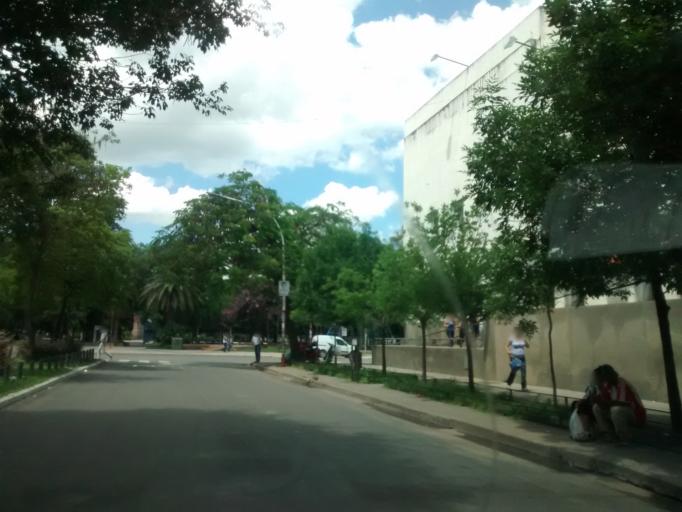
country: AR
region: Chaco
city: Resistencia
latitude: -27.4523
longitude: -58.9877
